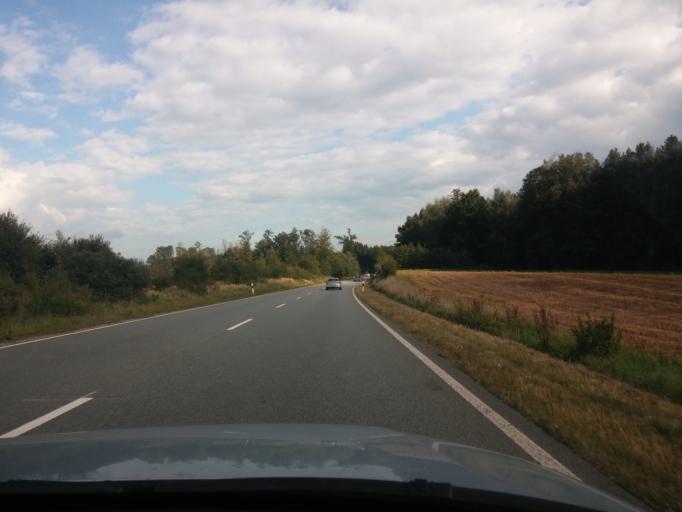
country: DE
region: Bavaria
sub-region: Upper Bavaria
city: Grafing bei Munchen
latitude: 48.0641
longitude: 11.9386
